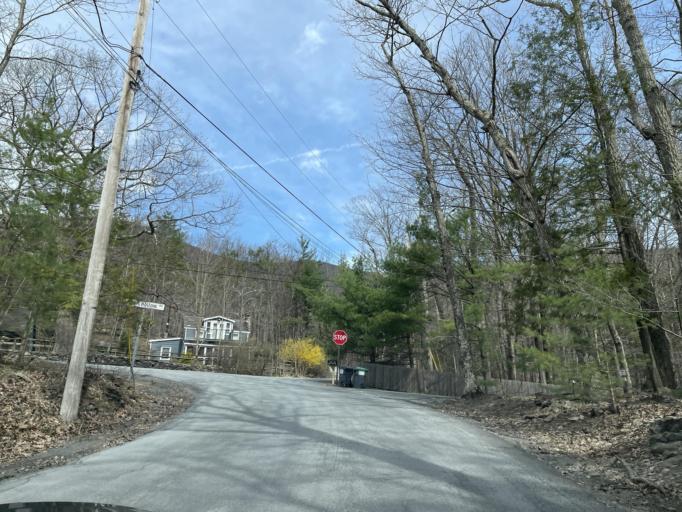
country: US
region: New York
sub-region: Ulster County
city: Woodstock
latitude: 42.0638
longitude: -74.0913
